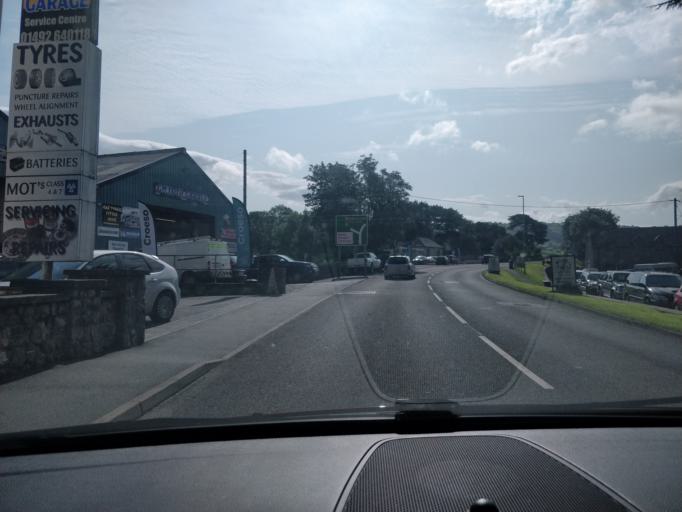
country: GB
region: Wales
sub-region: Conwy
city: Llanrwst
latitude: 53.1368
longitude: -3.7960
